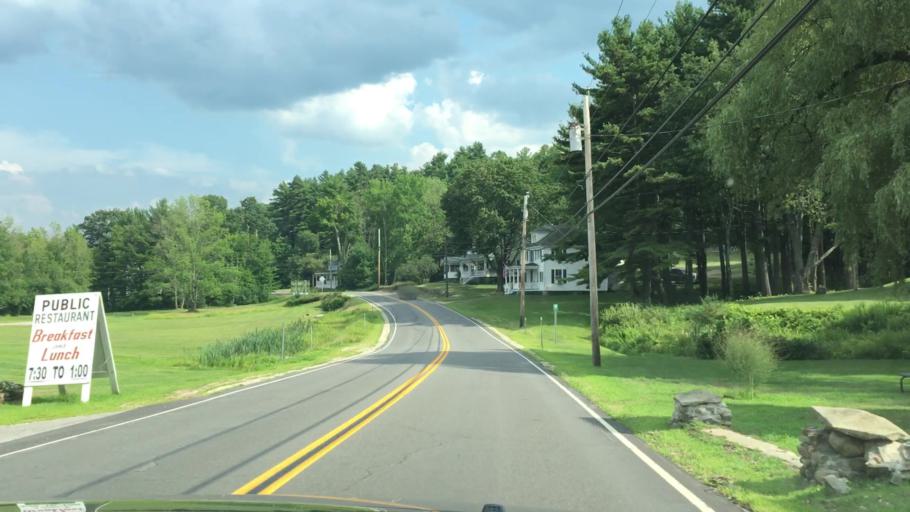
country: US
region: New Hampshire
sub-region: Belknap County
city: Gilford
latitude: 43.5629
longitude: -71.3354
